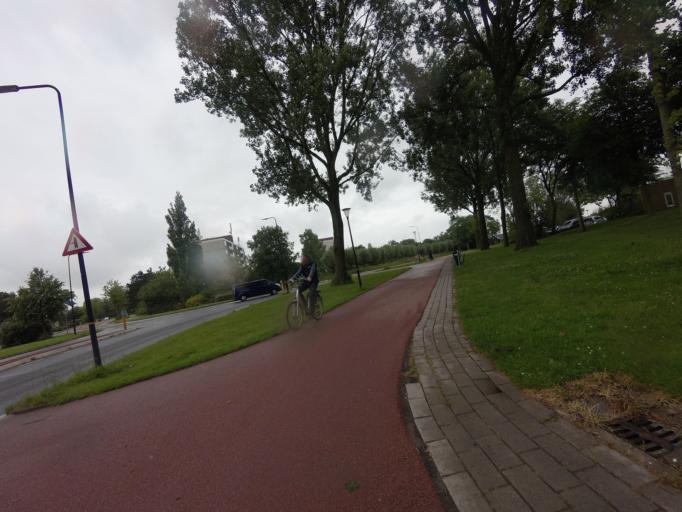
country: NL
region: North Holland
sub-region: Gemeente Schagen
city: Schagen
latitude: 52.7947
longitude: 4.8015
